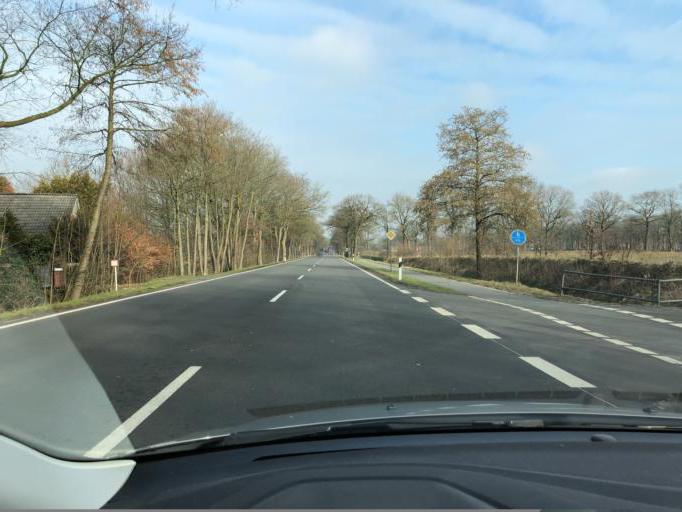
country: DE
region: Lower Saxony
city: Hesel
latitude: 53.3326
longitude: 7.6040
